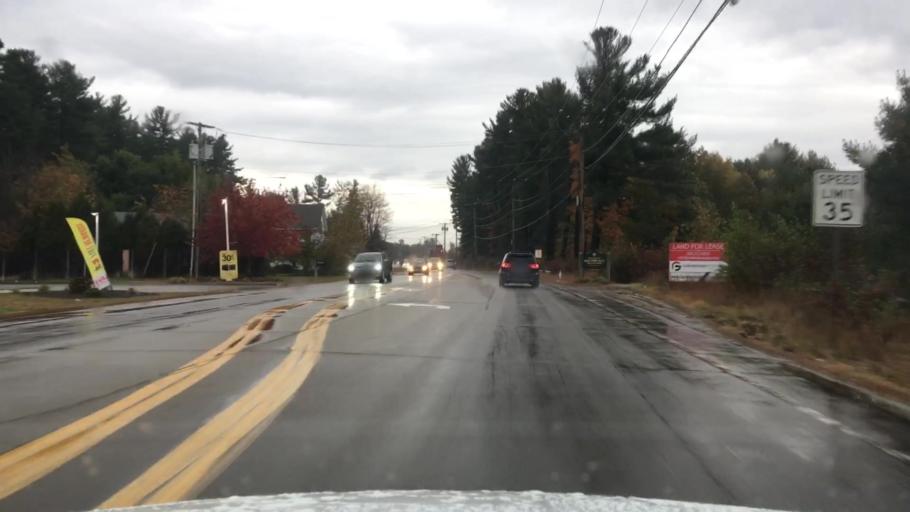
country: US
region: New Hampshire
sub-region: Strafford County
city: Dover
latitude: 43.2322
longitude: -70.8971
